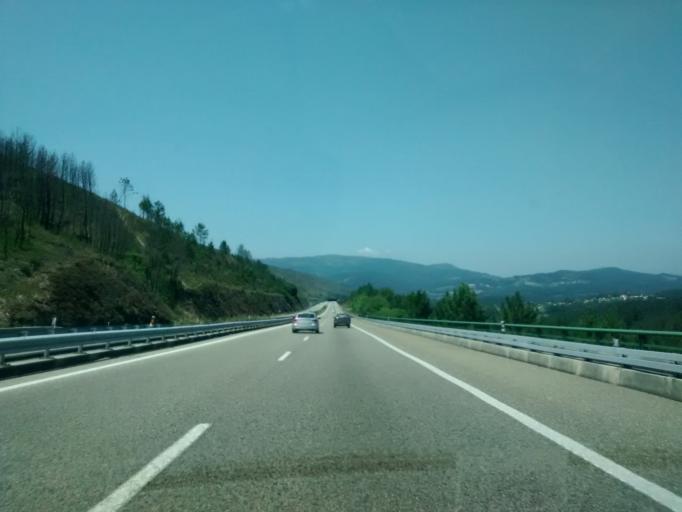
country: PT
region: Viana do Castelo
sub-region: Paredes de Coura
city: Paredes de Coura
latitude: 41.8599
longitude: -8.6414
